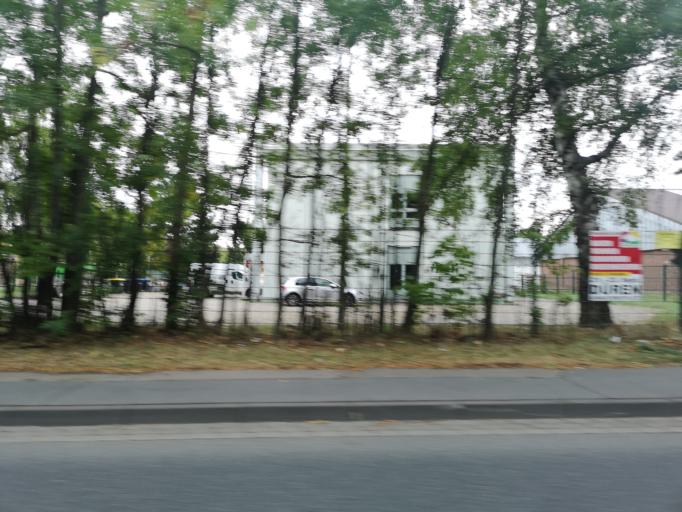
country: DE
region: North Rhine-Westphalia
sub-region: Regierungsbezirk Koln
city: Dueren
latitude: 50.7842
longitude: 6.4886
